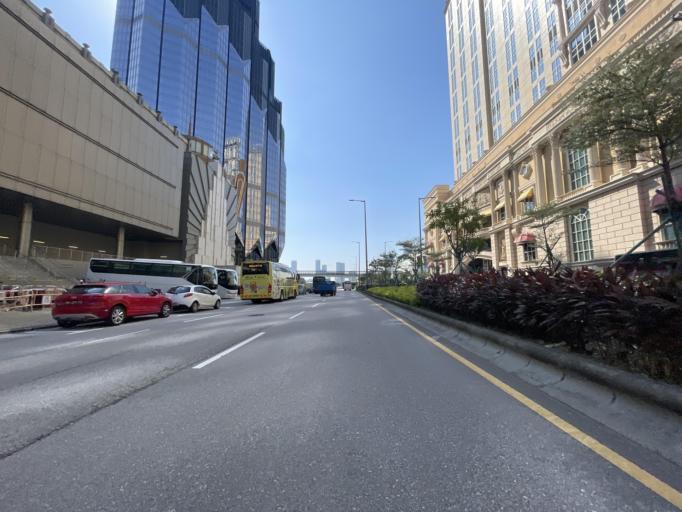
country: MO
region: Macau
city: Macau
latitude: 22.1425
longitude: 113.5612
